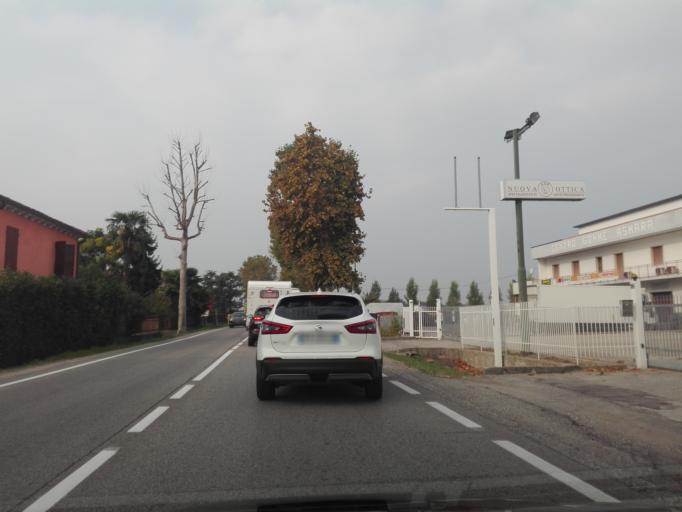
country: IT
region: Veneto
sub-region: Provincia di Verona
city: Castelnuovo del Garda
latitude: 45.4381
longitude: 10.7556
